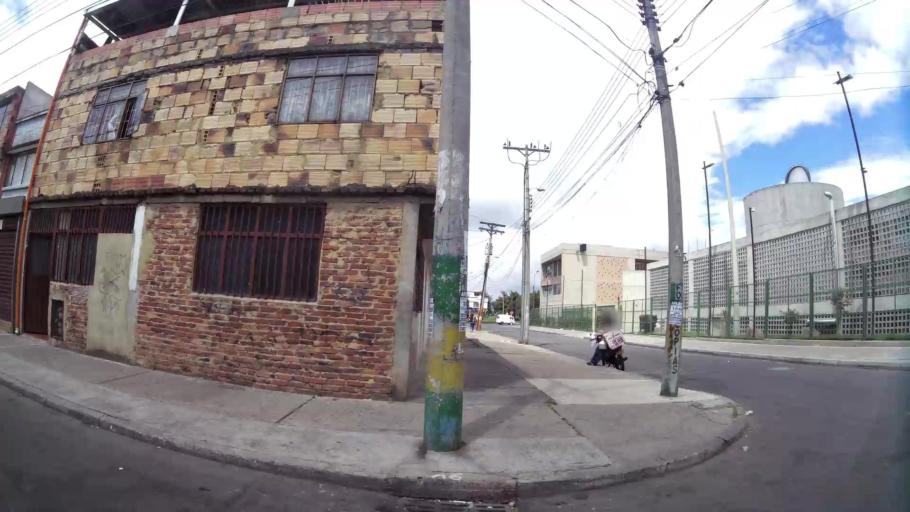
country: CO
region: Bogota D.C.
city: Bogota
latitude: 4.6034
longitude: -74.1240
